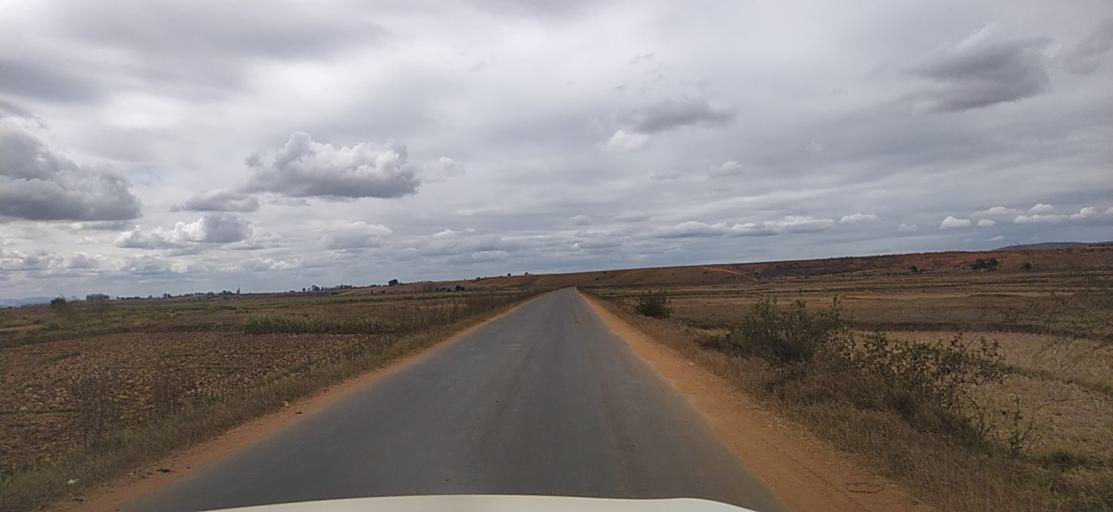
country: MG
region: Alaotra Mangoro
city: Ambatondrazaka
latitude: -17.9208
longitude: 48.2577
